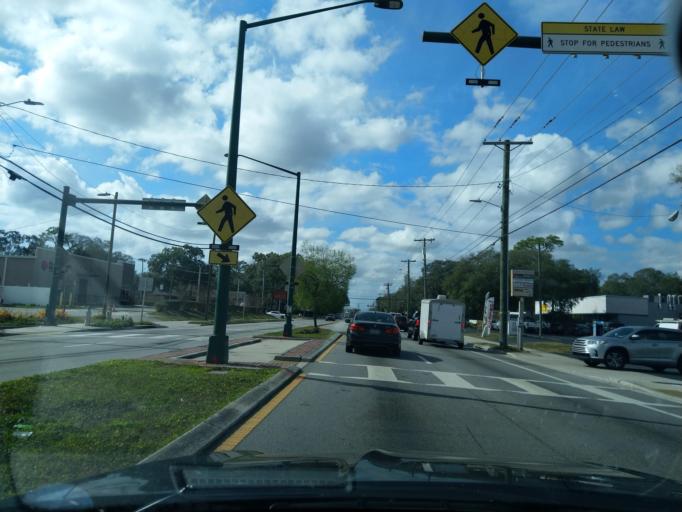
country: US
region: Florida
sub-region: Hillsborough County
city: University
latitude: 28.0693
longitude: -82.4375
